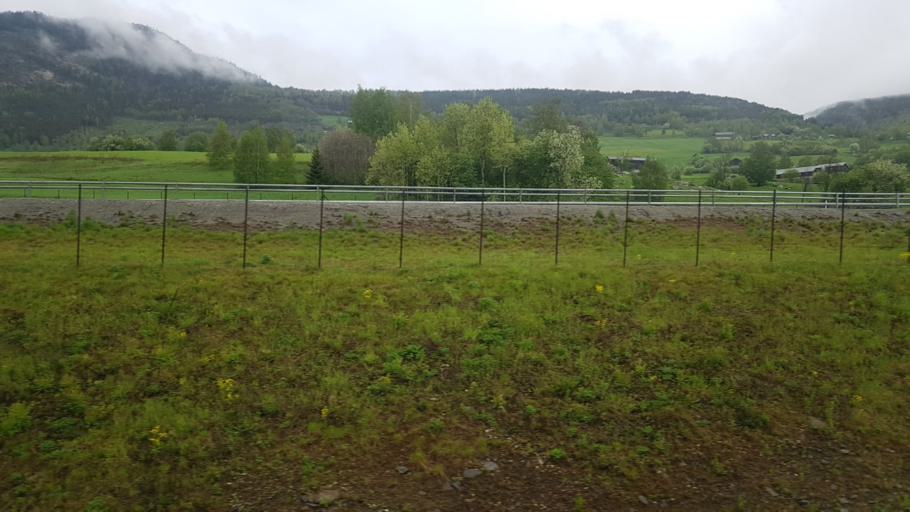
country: NO
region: Oppland
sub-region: Sor-Fron
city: Hundorp
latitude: 61.5712
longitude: 9.8671
